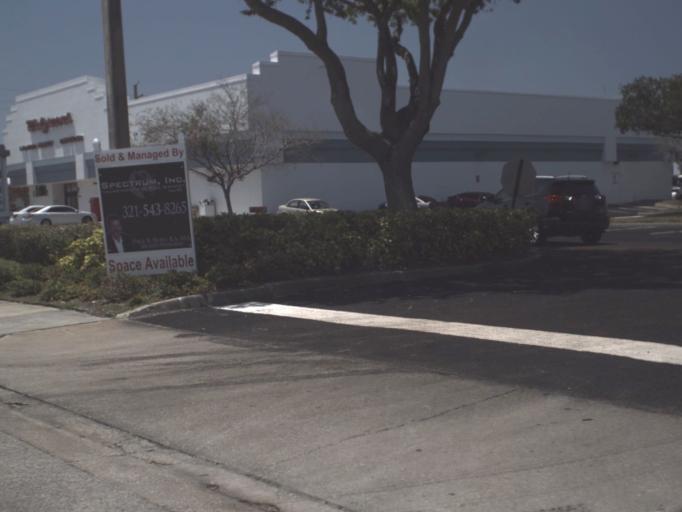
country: US
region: Florida
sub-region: Brevard County
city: June Park
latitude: 28.0790
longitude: -80.6715
